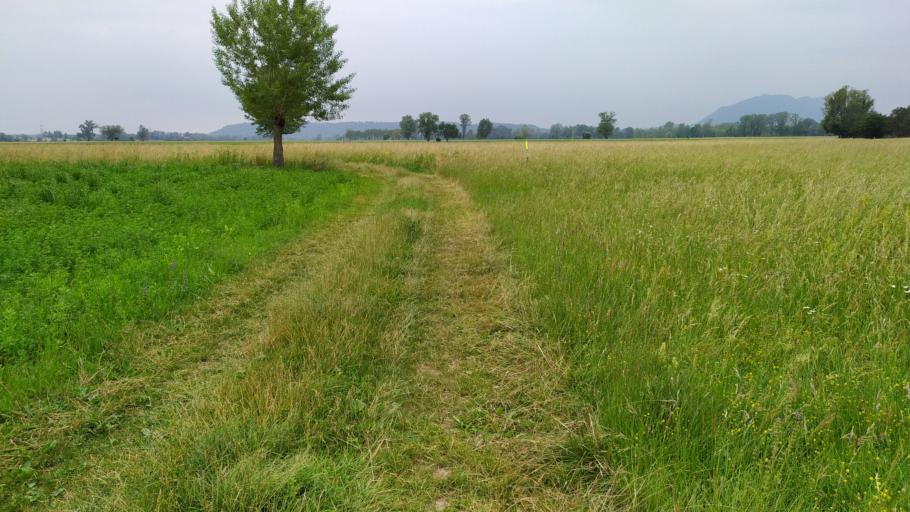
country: IT
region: Friuli Venezia Giulia
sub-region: Provincia di Udine
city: Osoppo
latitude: 46.2357
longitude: 13.0657
